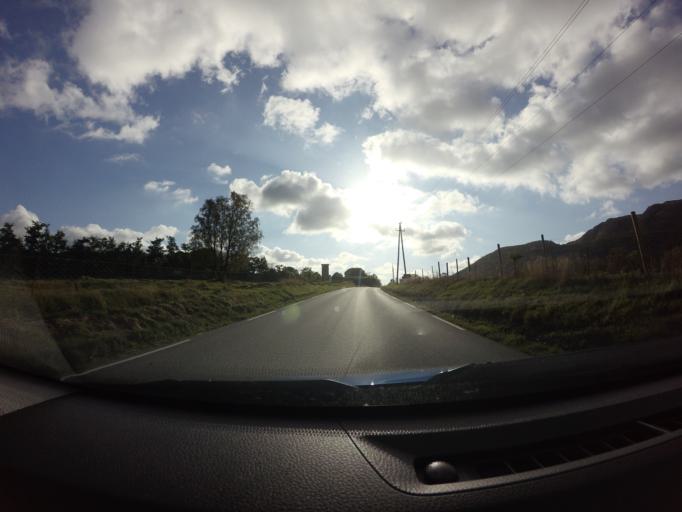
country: NO
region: Rogaland
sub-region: Sandnes
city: Hommersak
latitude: 58.8574
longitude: 5.9127
